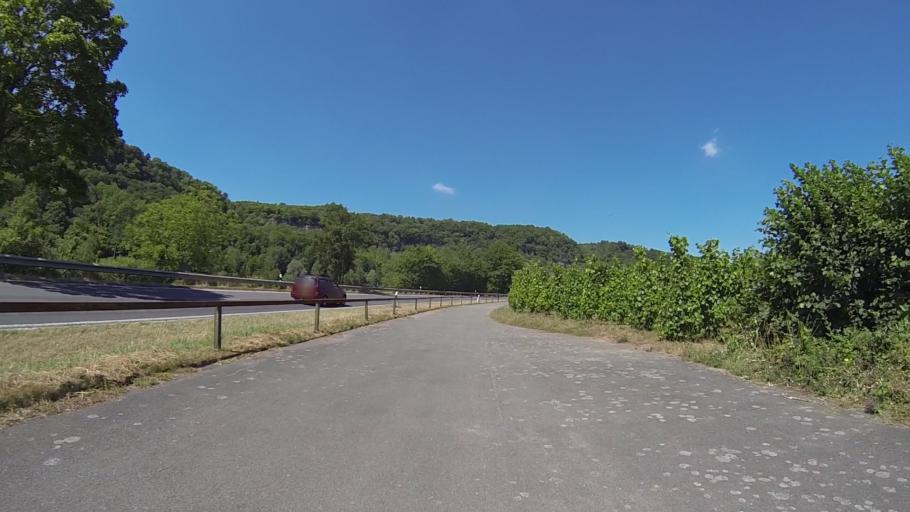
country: DE
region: Rheinland-Pfalz
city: Wellen
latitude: 49.6620
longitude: 6.4275
